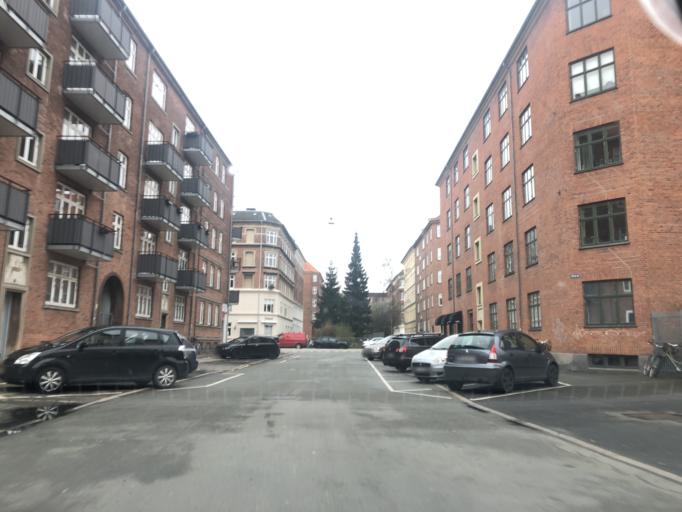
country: DK
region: Capital Region
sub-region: Kobenhavn
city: Christianshavn
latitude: 55.6551
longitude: 12.6118
